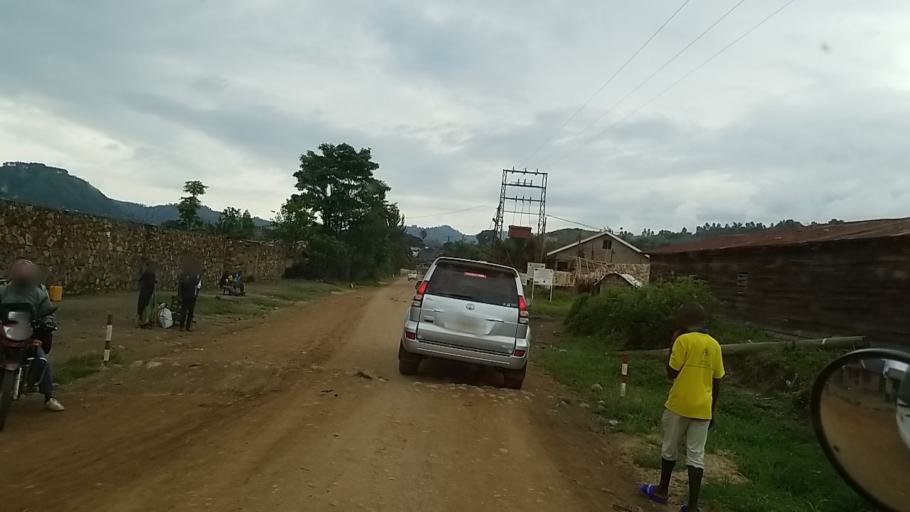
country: CD
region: Nord Kivu
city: Sake
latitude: -1.6855
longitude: 29.0161
